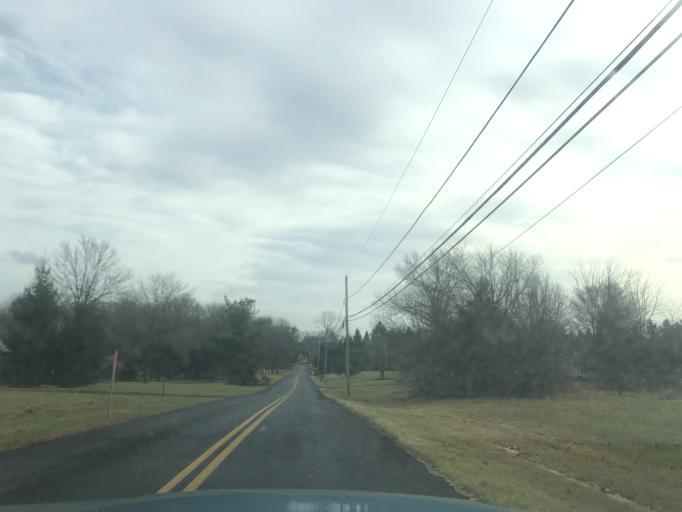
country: US
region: Pennsylvania
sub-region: Montgomery County
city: Harleysville
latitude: 40.2599
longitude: -75.4036
